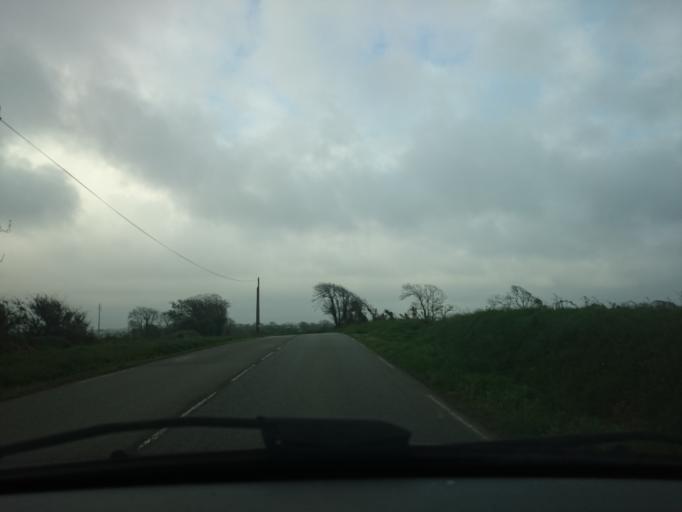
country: FR
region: Brittany
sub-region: Departement du Finistere
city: Lanrivoare
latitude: 48.4824
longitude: -4.6639
